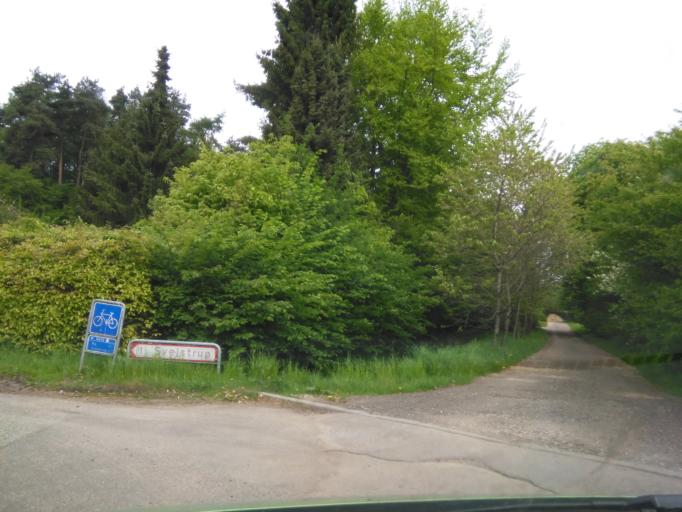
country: DK
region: Central Jutland
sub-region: Skanderborg Kommune
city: Skanderborg
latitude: 56.0672
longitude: 9.8538
